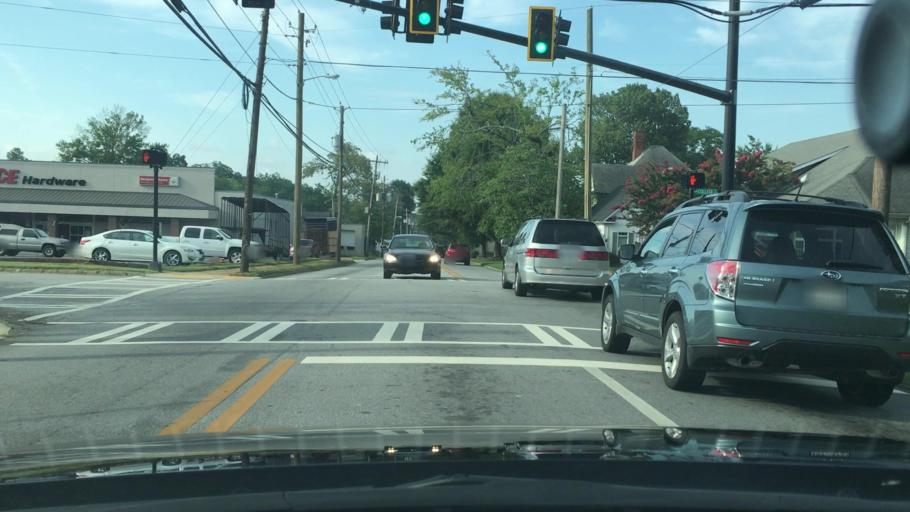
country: US
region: Georgia
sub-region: Spalding County
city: Griffin
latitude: 33.2446
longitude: -84.2656
